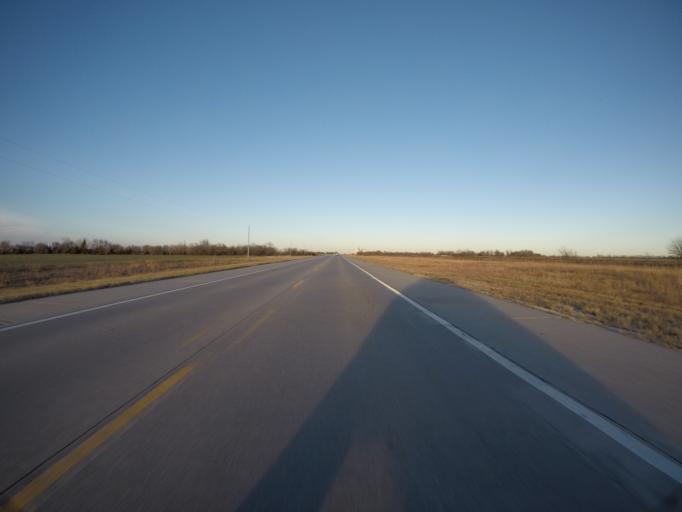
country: US
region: Kansas
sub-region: Harvey County
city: North Newton
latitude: 38.1045
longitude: -97.2715
